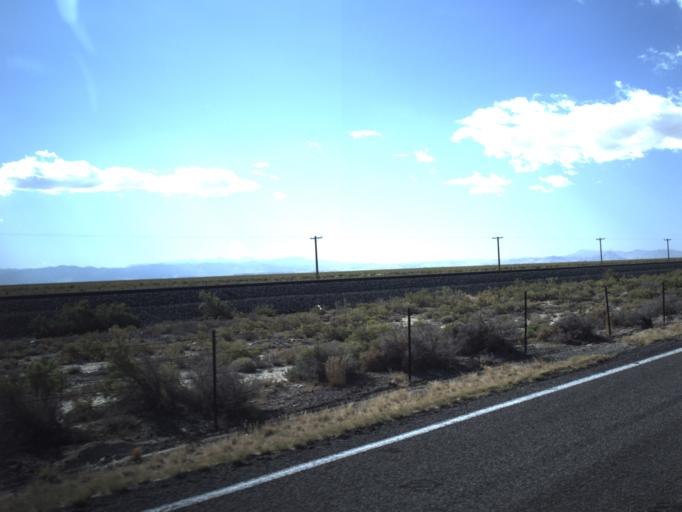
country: US
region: Utah
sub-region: Millard County
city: Delta
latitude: 39.1455
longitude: -112.7221
